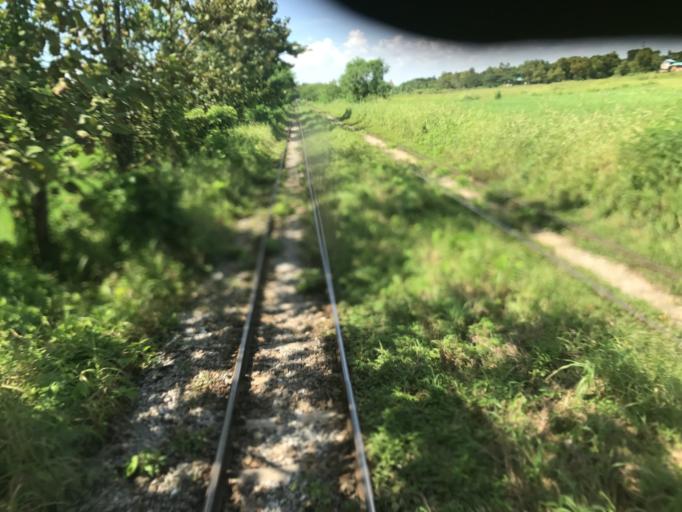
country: MM
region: Yangon
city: Yangon
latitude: 16.9656
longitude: 96.0858
